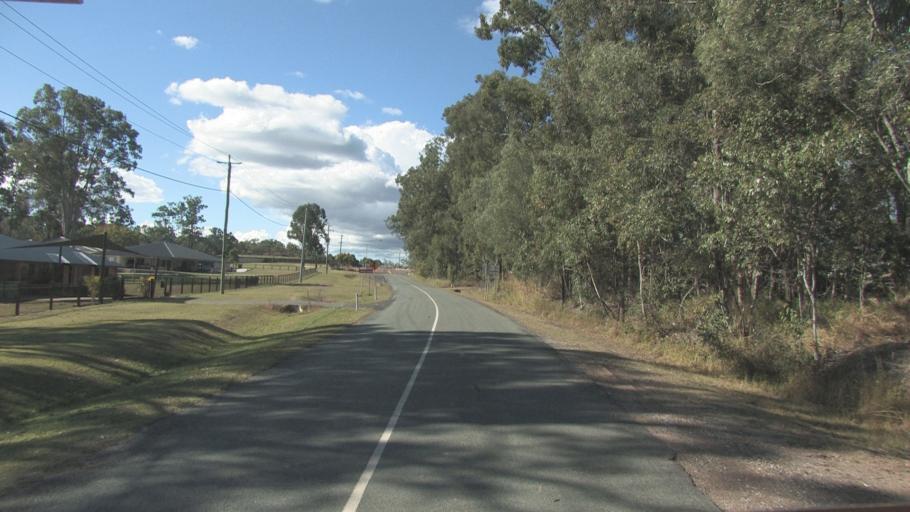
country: AU
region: Queensland
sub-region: Logan
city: Chambers Flat
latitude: -27.7891
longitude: 153.0982
